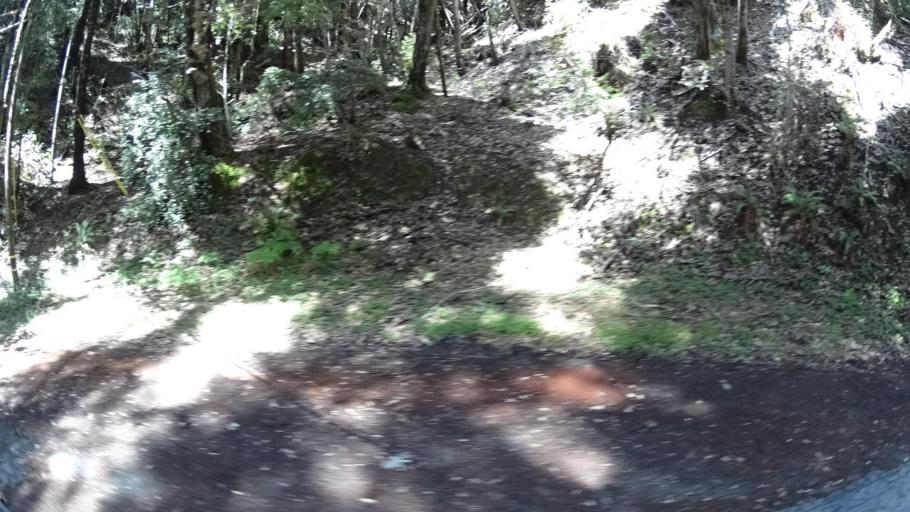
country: US
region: California
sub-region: Humboldt County
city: Blue Lake
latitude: 40.7617
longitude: -123.9527
